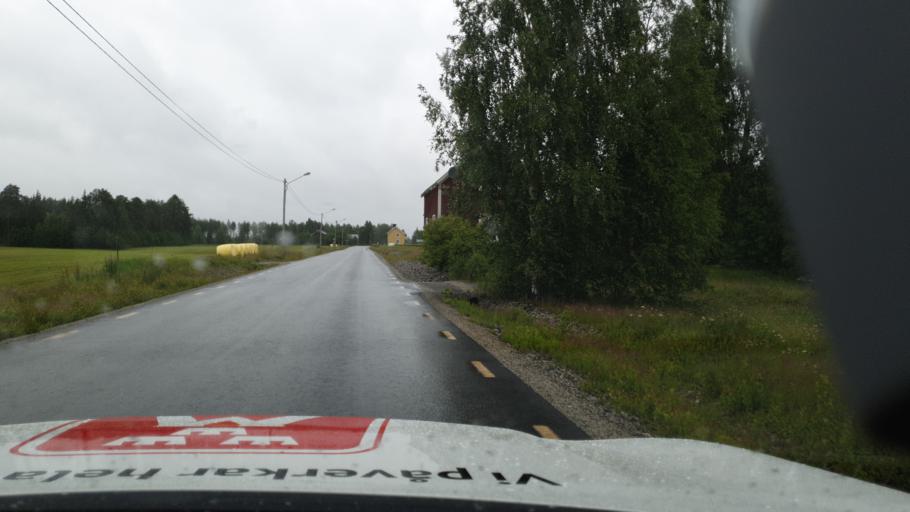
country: SE
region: Vaesterbotten
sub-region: Norsjo Kommun
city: Norsjoe
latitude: 64.5390
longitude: 19.3389
